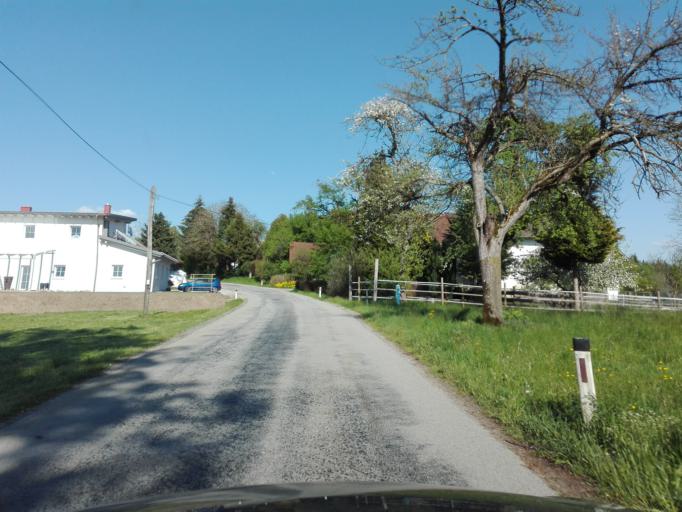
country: DE
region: Bavaria
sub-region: Lower Bavaria
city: Obernzell
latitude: 48.4992
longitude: 13.5846
